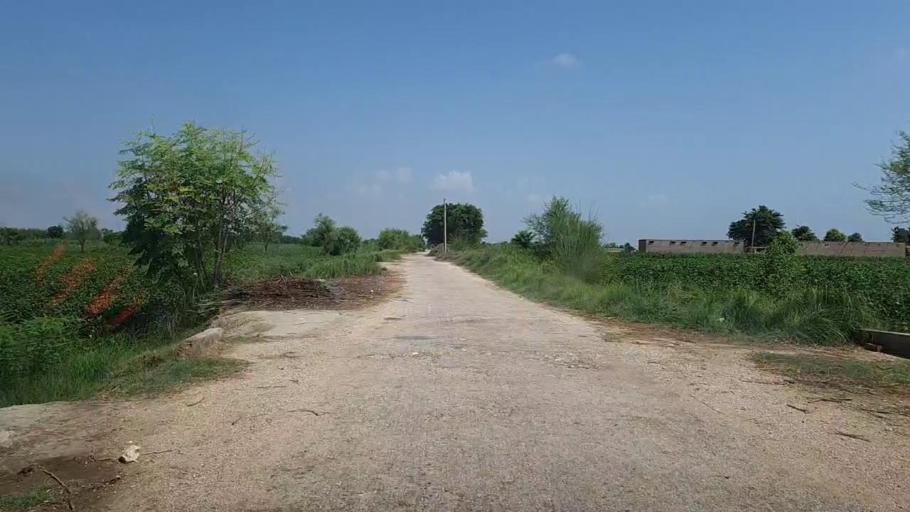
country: PK
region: Sindh
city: Bhiria
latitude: 26.8763
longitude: 68.2475
